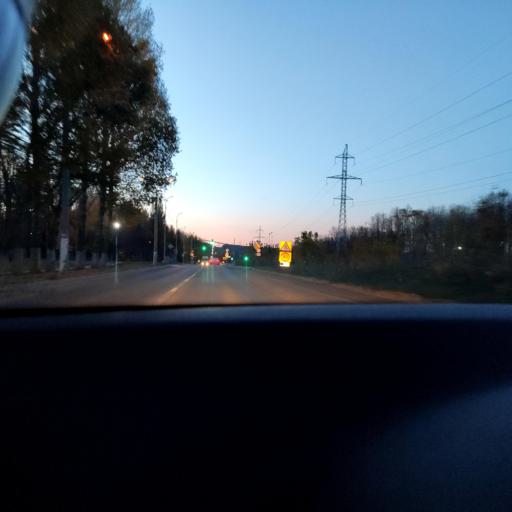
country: RU
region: Samara
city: Petra-Dubrava
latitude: 53.3066
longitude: 50.2796
